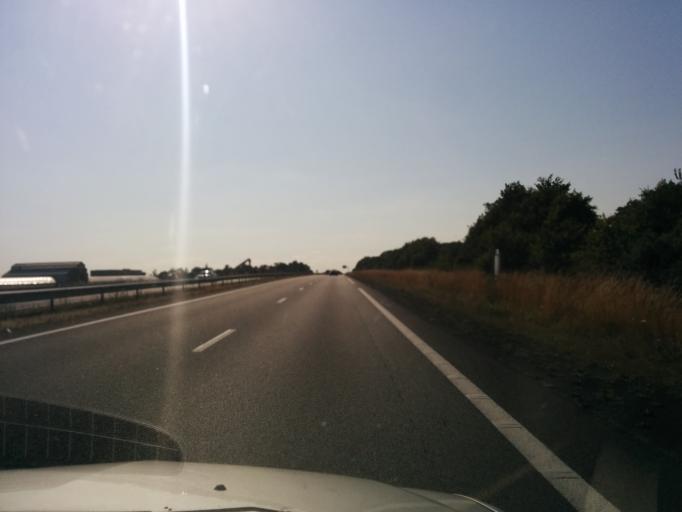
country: FR
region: Pays de la Loire
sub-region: Departement de Maine-et-Loire
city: Villedieu-la-Blouere
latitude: 47.1198
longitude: -1.0850
